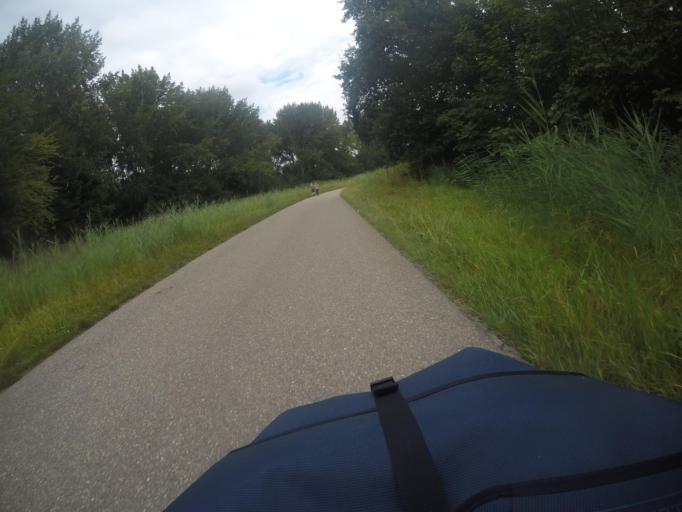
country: NL
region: Flevoland
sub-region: Gemeente Almere
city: Almere Stad
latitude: 52.3782
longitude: 5.1717
